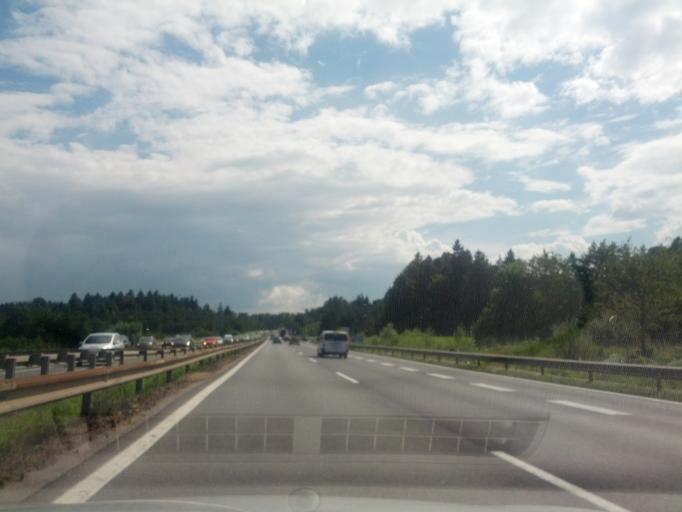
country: SI
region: Ljubljana
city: Ljubljana
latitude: 46.0593
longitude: 14.4543
